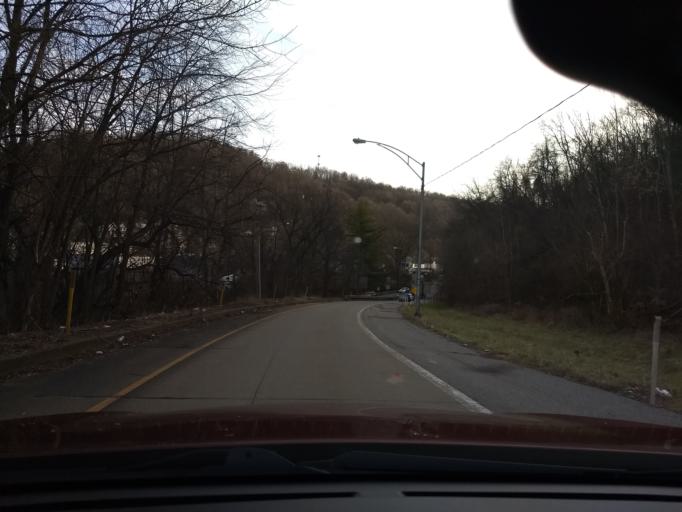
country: US
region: Pennsylvania
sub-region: Allegheny County
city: West Homestead
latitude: 40.3848
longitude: -79.9336
